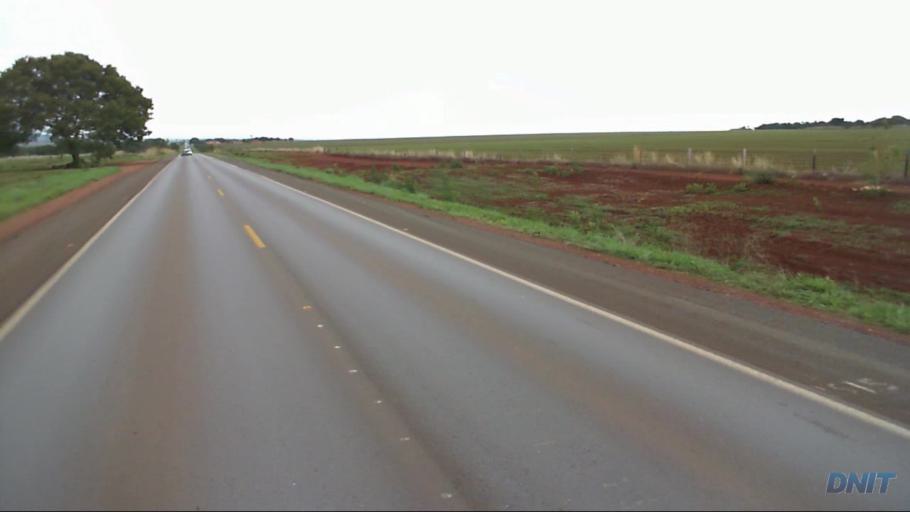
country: BR
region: Goias
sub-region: Barro Alto
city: Barro Alto
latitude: -14.8509
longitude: -49.0253
